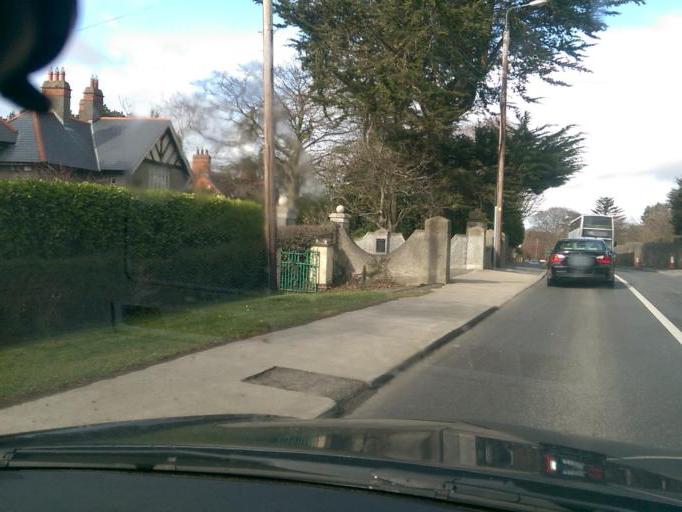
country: IE
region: Leinster
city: Malahide
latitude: 53.4458
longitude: -6.1527
